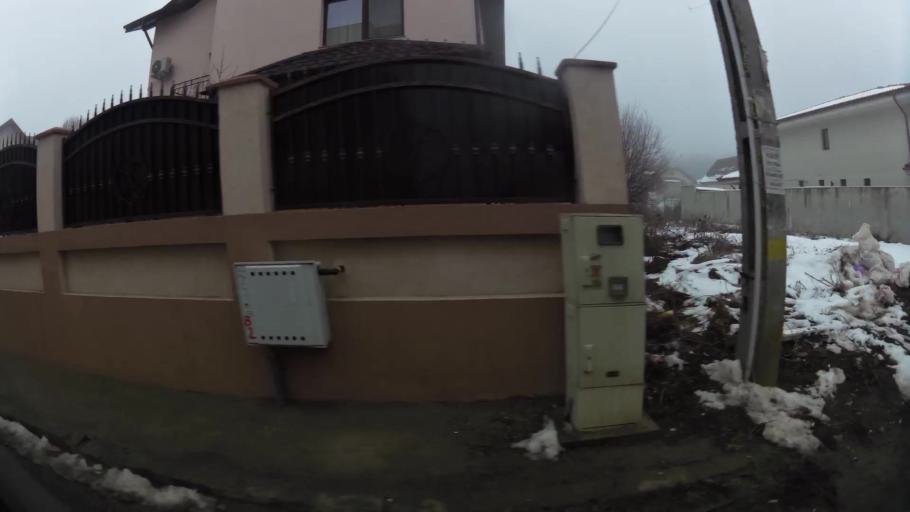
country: RO
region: Ilfov
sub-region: Comuna Chiajna
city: Rosu
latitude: 44.4562
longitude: 25.9968
